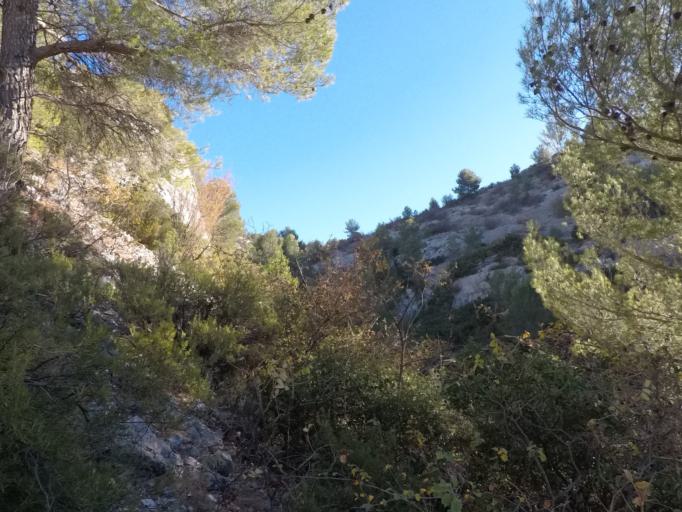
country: FR
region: Provence-Alpes-Cote d'Azur
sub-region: Departement des Bouches-du-Rhone
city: La Penne-sur-Huveaune
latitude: 43.2677
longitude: 5.5100
